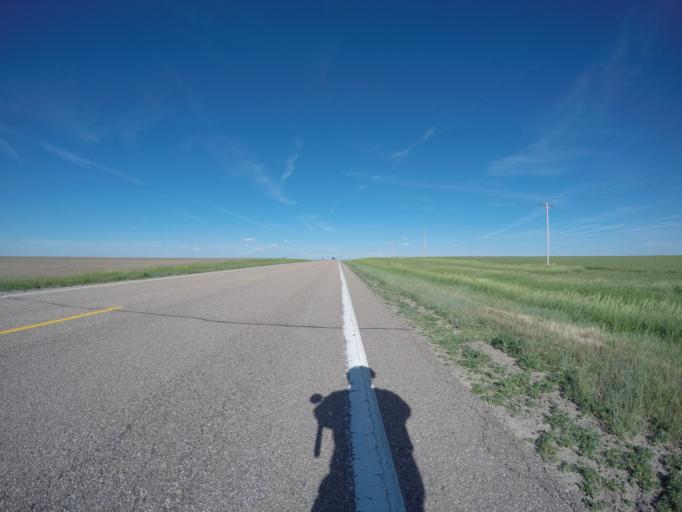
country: US
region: Kansas
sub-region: Cheyenne County
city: Saint Francis
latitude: 39.7565
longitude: -102.0110
